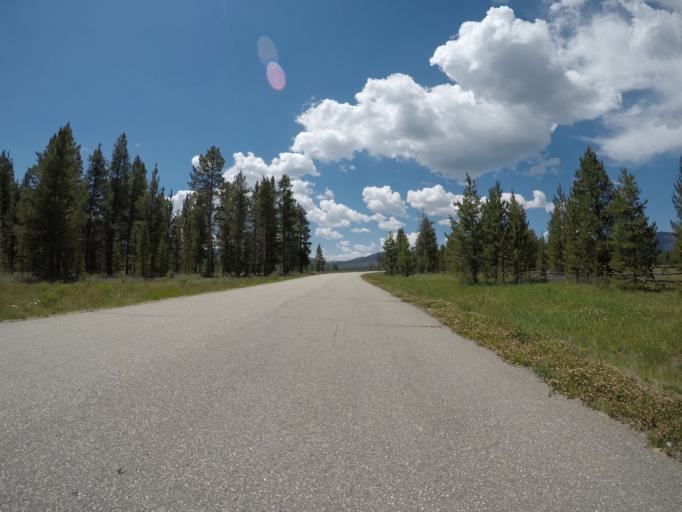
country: US
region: Colorado
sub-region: Grand County
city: Fraser
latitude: 39.9675
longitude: -105.8591
